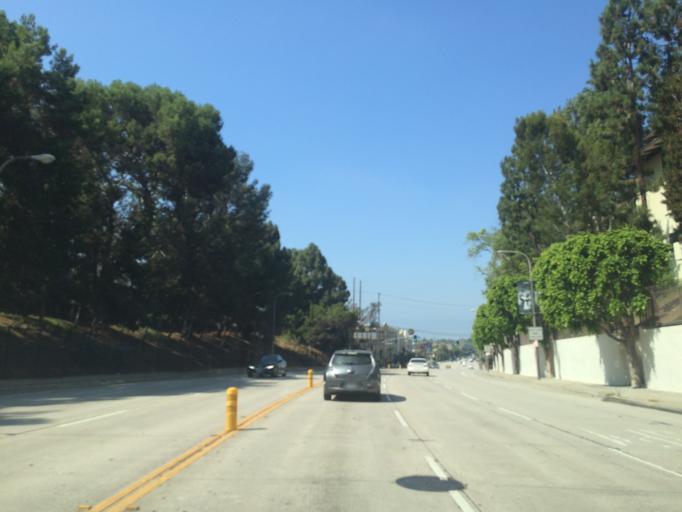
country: US
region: California
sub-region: Los Angeles County
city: Century City
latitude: 34.0541
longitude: -118.4151
